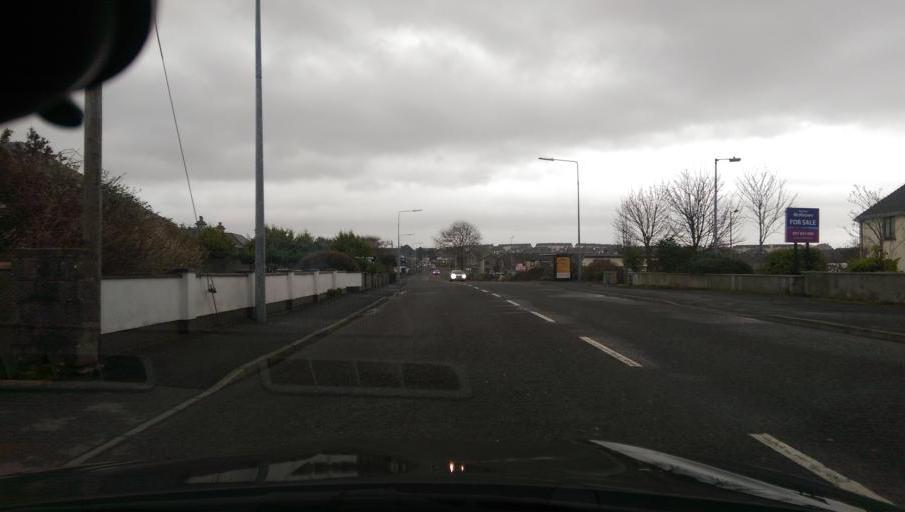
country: IE
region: Connaught
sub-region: County Galway
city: Gaillimh
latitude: 53.2887
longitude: -9.0091
